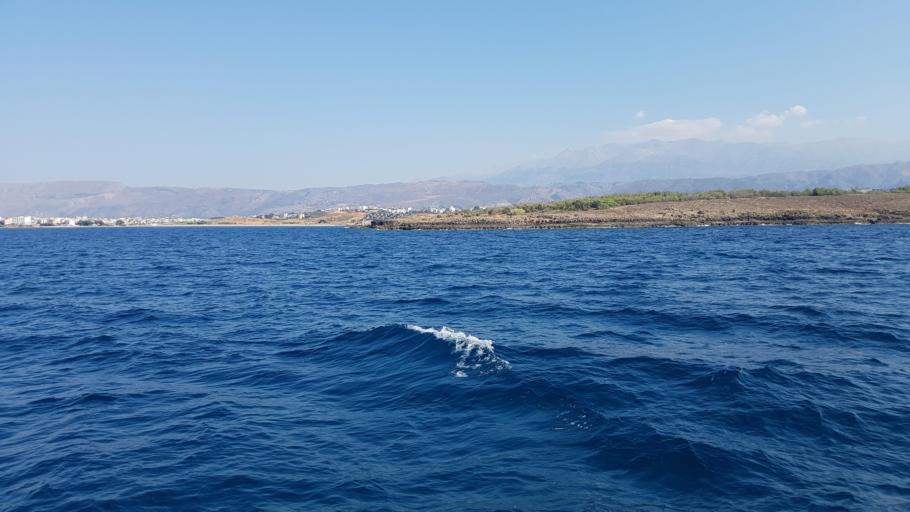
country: GR
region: Crete
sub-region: Nomos Chanias
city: Daratsos
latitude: 35.5214
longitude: 23.9869
